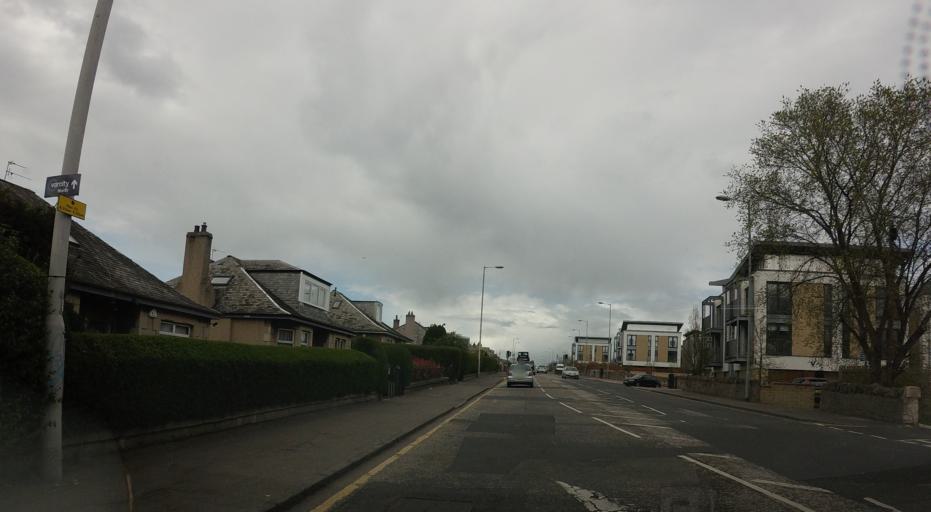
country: GB
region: Scotland
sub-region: Edinburgh
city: Edinburgh
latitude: 55.9655
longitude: -3.2340
